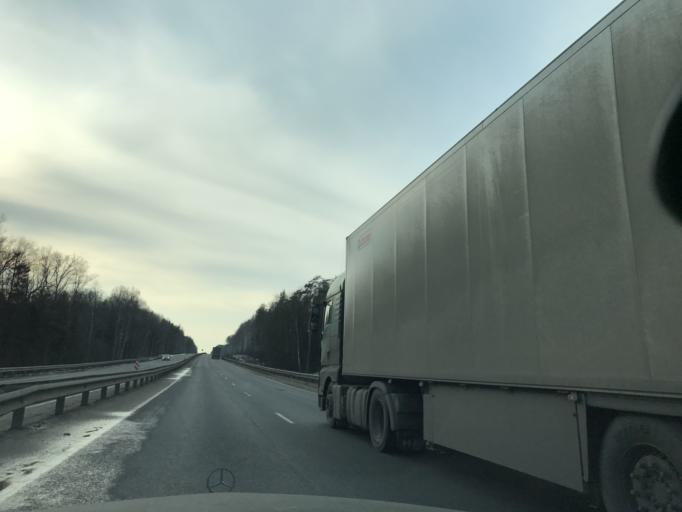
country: RU
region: Vladimir
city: Kameshkovo
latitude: 56.1970
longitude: 41.0060
